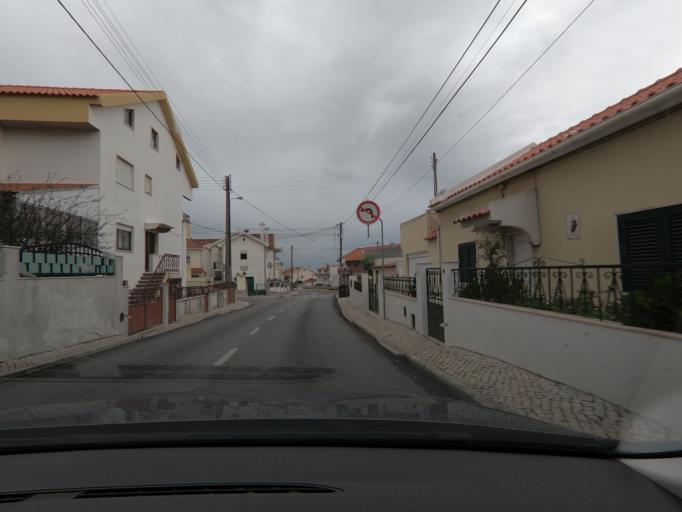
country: PT
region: Lisbon
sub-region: Cascais
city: Sao Domingos de Rana
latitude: 38.7162
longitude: -9.3329
